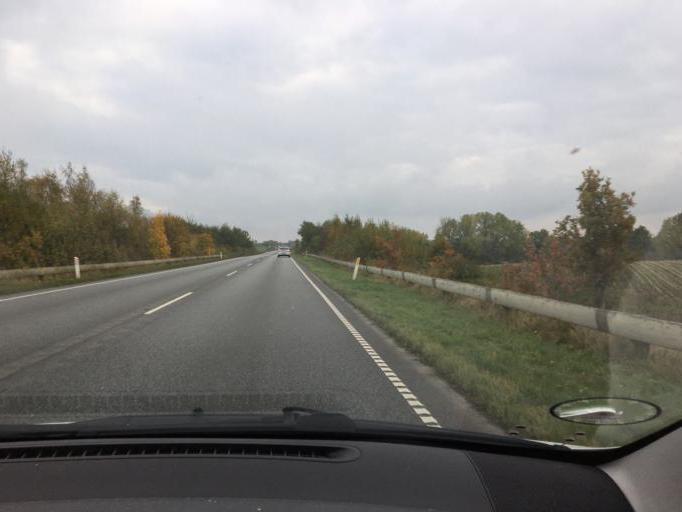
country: DK
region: South Denmark
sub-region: Fredericia Kommune
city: Fredericia
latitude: 55.6155
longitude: 9.7494
